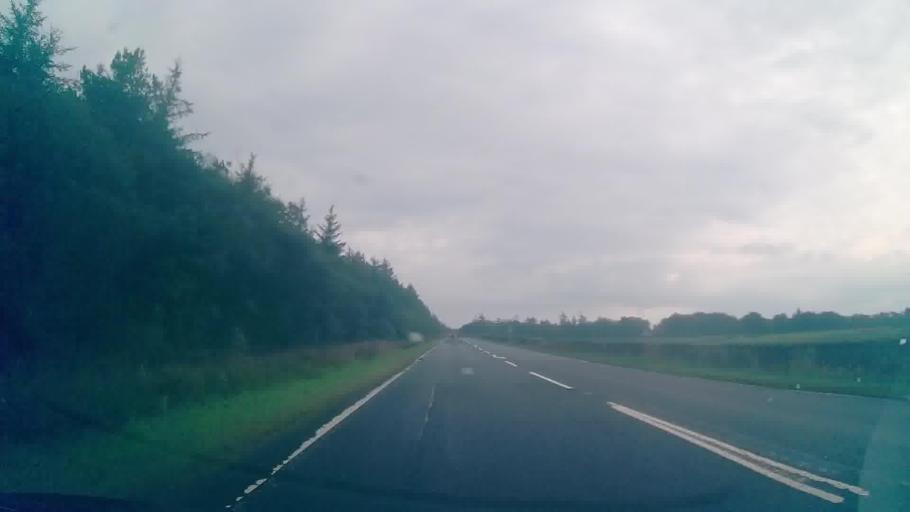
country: GB
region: Scotland
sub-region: Dumfries and Galloway
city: Annan
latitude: 55.0162
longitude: -3.3584
